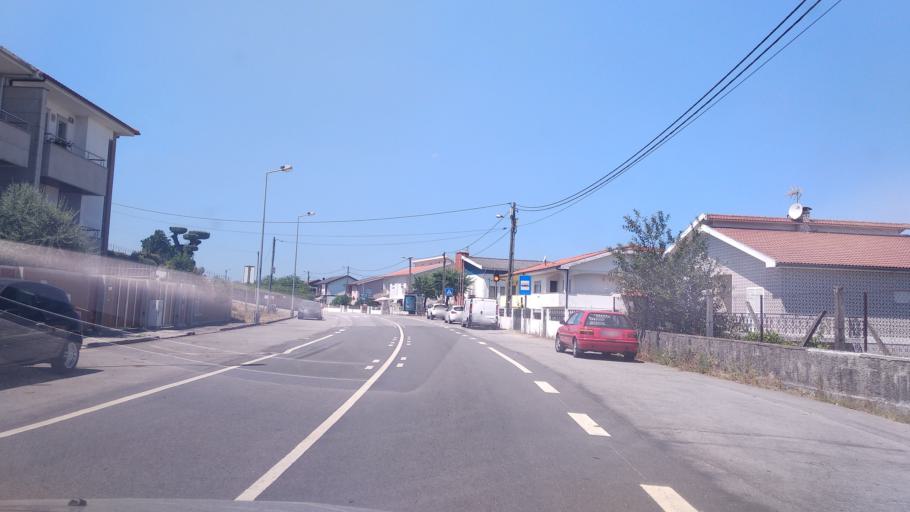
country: PT
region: Braga
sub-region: Braga
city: Adaufe
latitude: 41.5871
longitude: -8.3995
